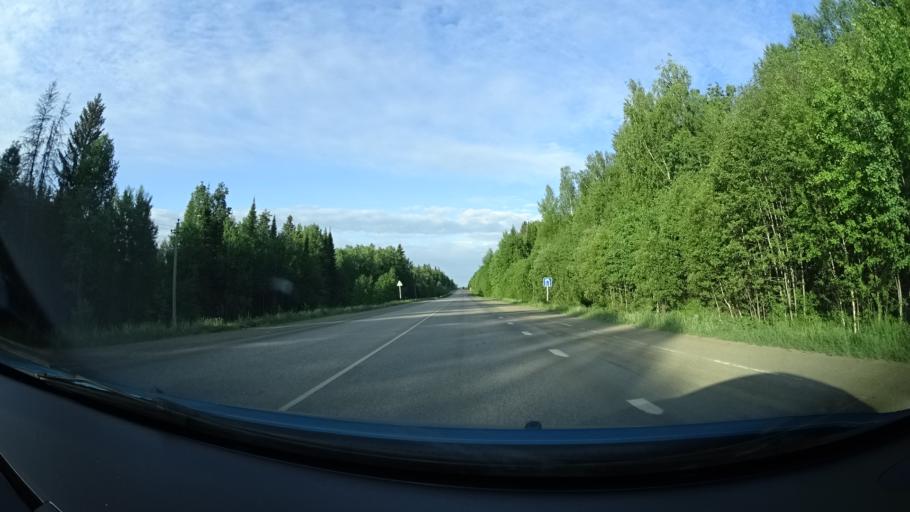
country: RU
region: Perm
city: Kultayevo
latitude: 57.8205
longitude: 55.8023
